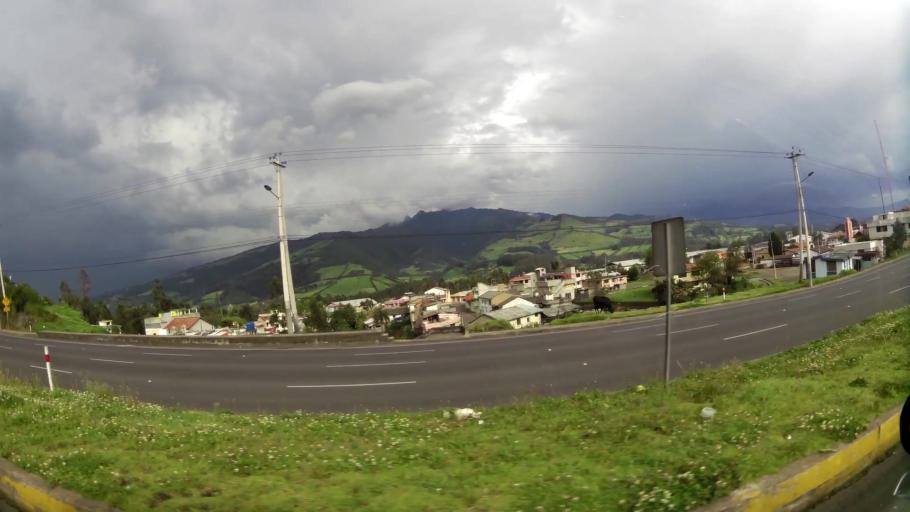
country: EC
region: Pichincha
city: Machachi
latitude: -0.4022
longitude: -78.5452
